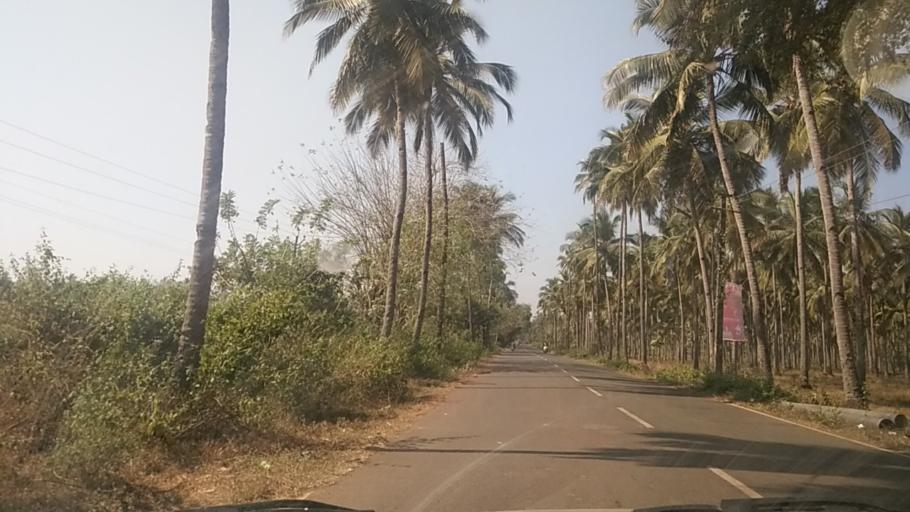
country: IN
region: Goa
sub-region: South Goa
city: Sanguem
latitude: 15.2286
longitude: 74.1788
